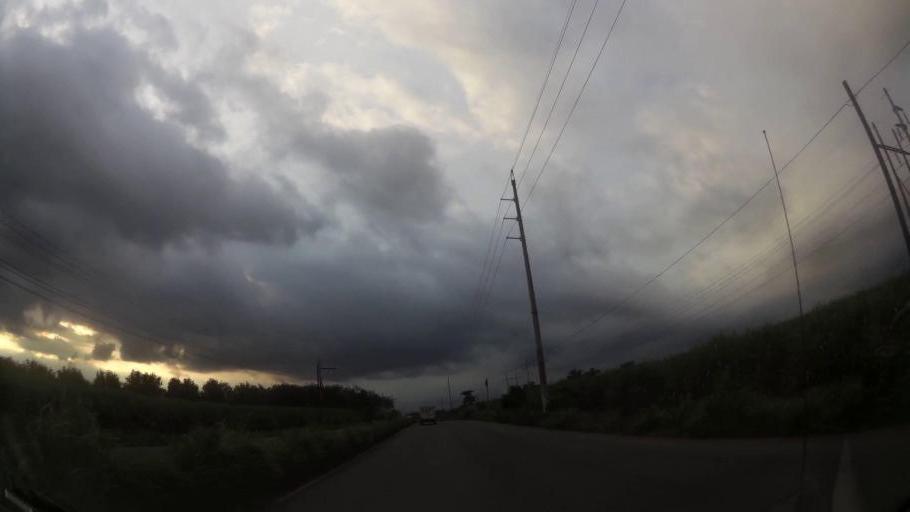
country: GT
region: Escuintla
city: Santa Lucia Cotzumalguapa
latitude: 14.3614
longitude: -91.0966
